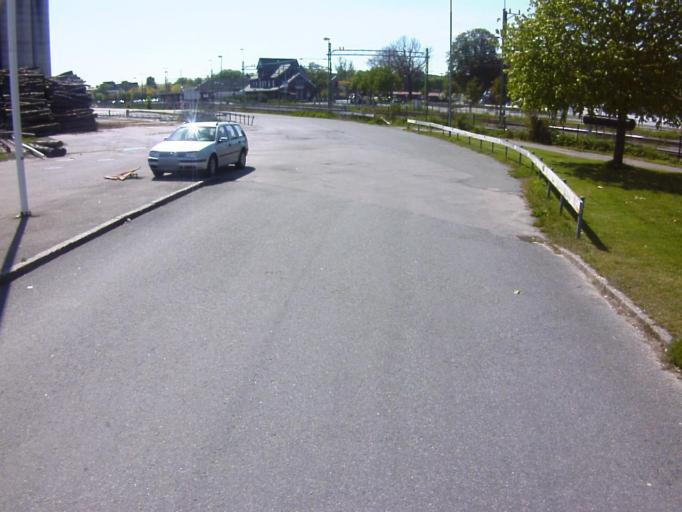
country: SE
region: Blekinge
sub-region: Solvesborgs Kommun
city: Soelvesborg
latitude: 56.0507
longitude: 14.5865
